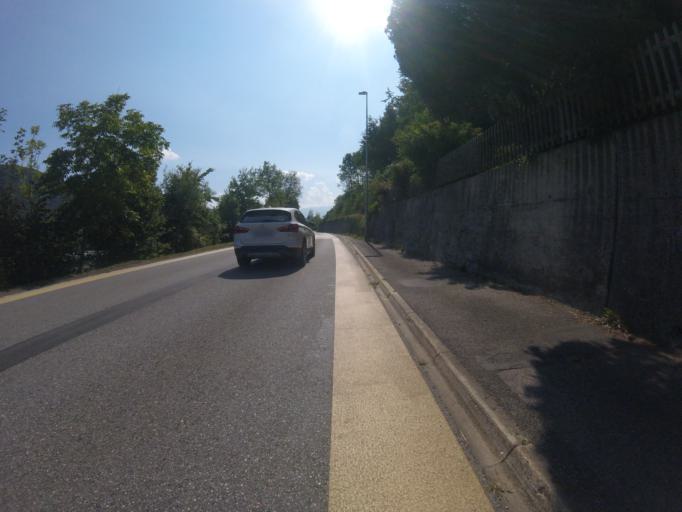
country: CH
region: Bern
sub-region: Bern-Mittelland District
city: Belp
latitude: 46.8858
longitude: 7.4957
